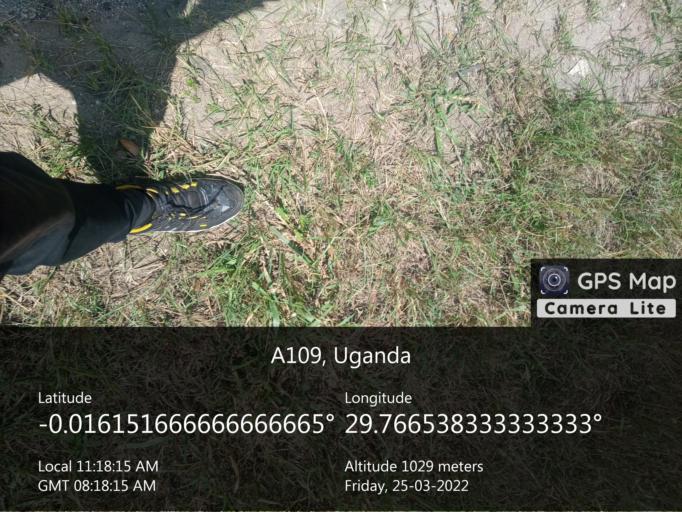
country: UG
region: Western Region
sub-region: Kasese District
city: Kilembe
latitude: -0.0162
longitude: 29.7665
